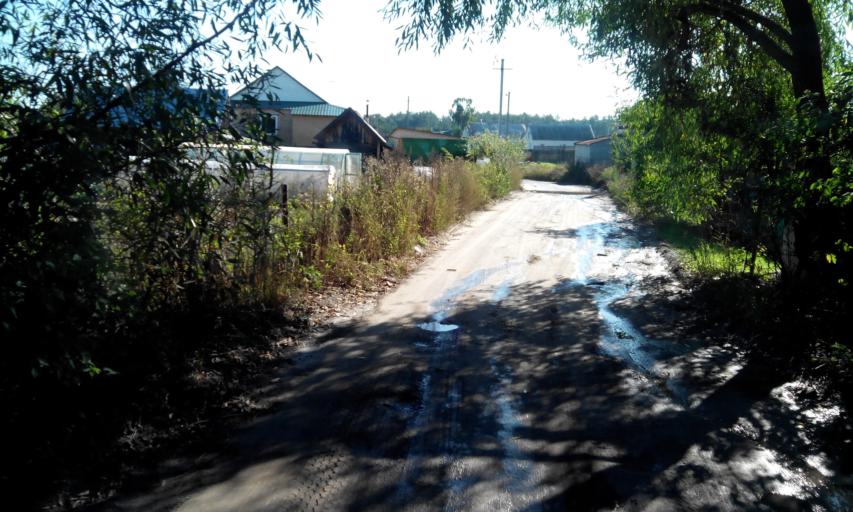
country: RU
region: Penza
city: Bessonovka
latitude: 53.2730
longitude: 45.1259
